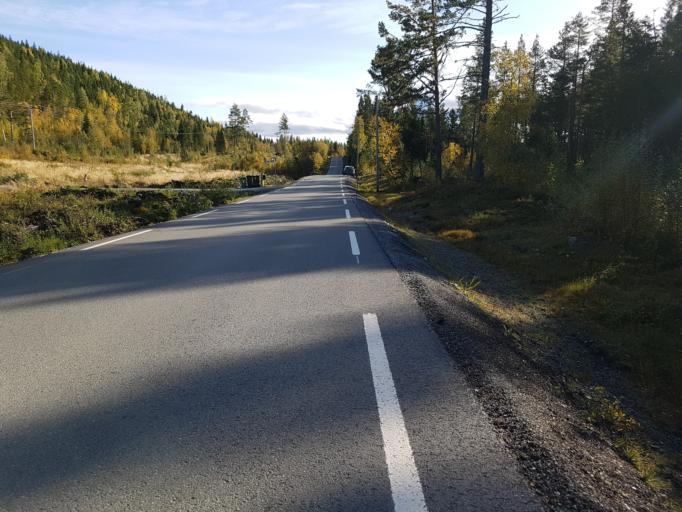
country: NO
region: Sor-Trondelag
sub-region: Malvik
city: Malvik
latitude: 63.3725
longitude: 10.6131
